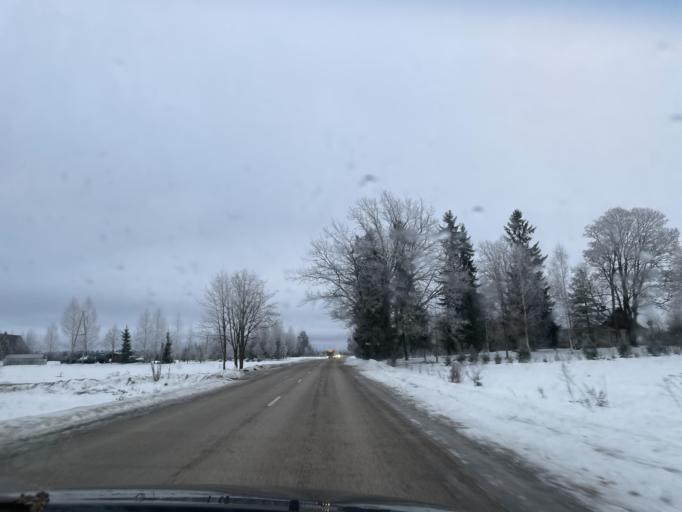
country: LV
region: Rezekne
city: Rezekne
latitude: 56.4968
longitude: 27.4131
